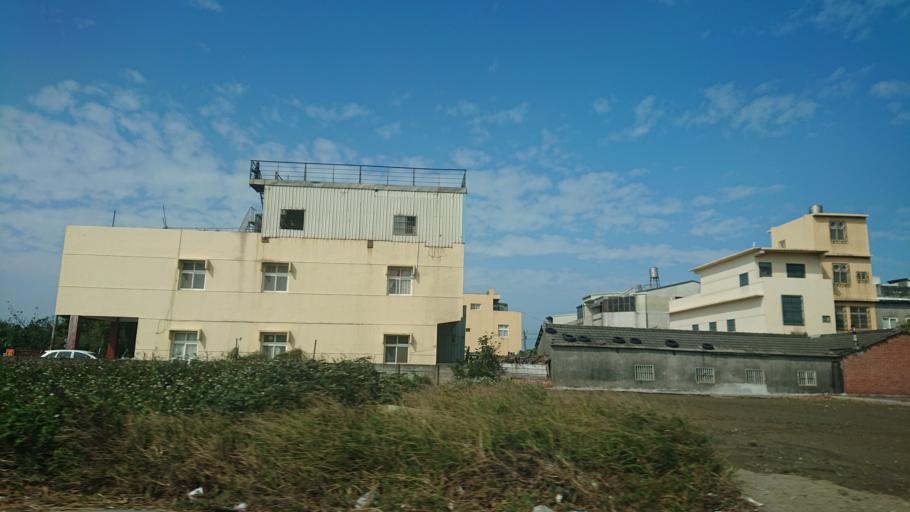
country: TW
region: Taiwan
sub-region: Changhua
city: Chang-hua
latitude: 23.9218
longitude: 120.3215
